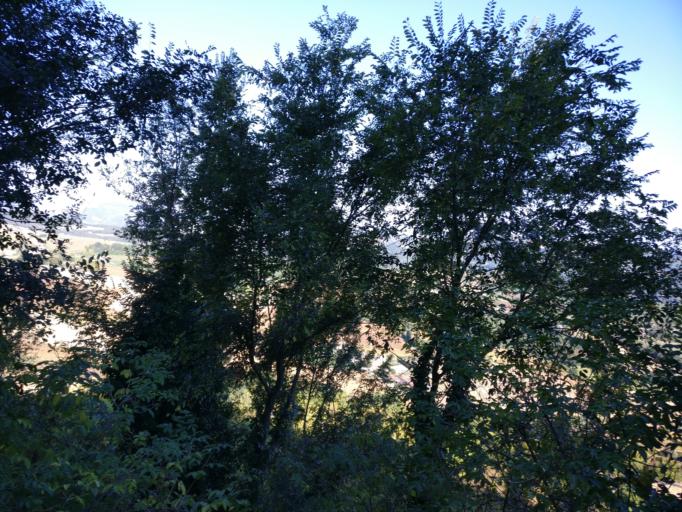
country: IT
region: The Marches
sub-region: Provincia di Ascoli Piceno
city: Montedinove
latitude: 42.9714
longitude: 13.5864
